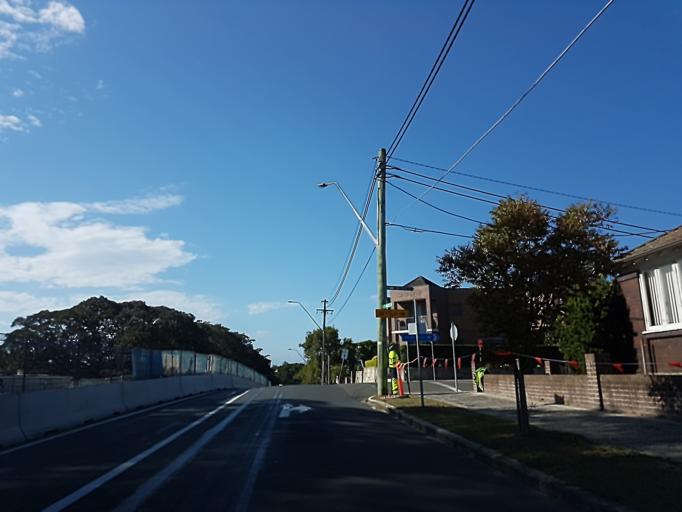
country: AU
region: New South Wales
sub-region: Randwick
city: Kingsford
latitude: -33.9151
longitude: 151.2351
